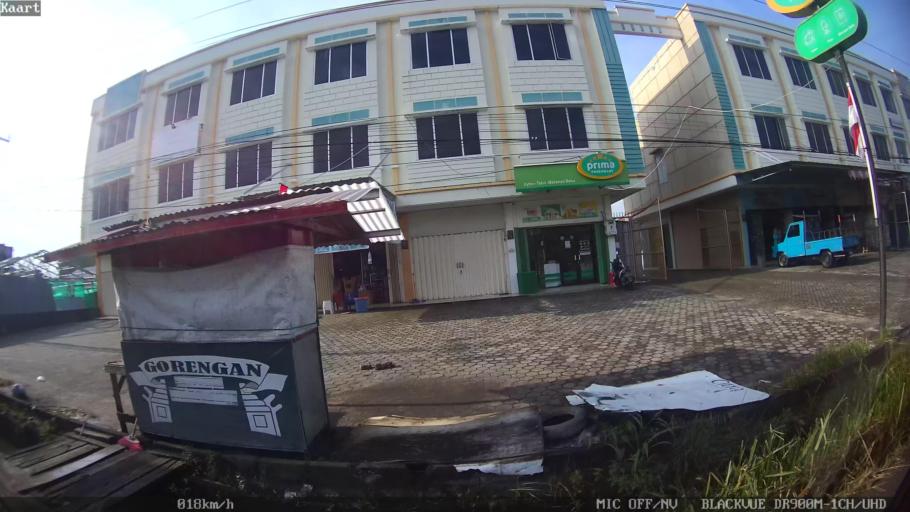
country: ID
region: Lampung
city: Kedaton
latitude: -5.3856
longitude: 105.3128
